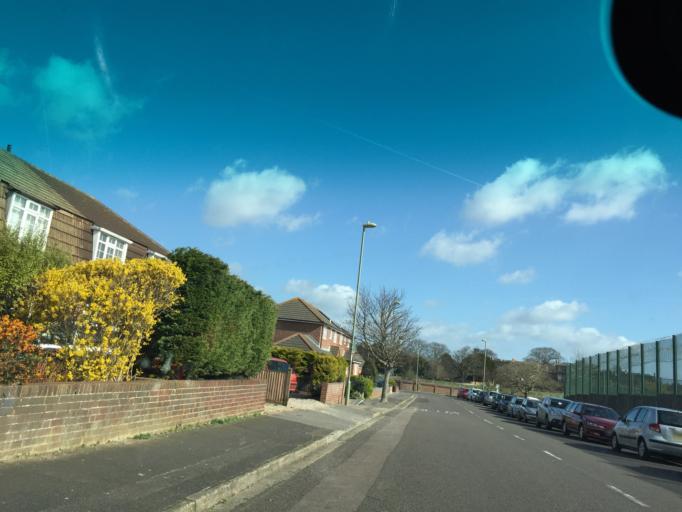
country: GB
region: England
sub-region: Hampshire
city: Gosport
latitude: 50.7814
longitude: -1.1304
